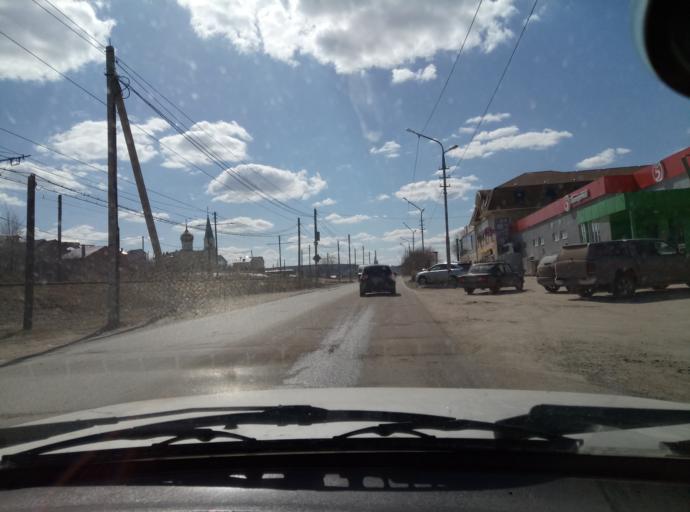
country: RU
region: Saratov
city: Sokolovyy
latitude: 51.5835
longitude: 45.9019
